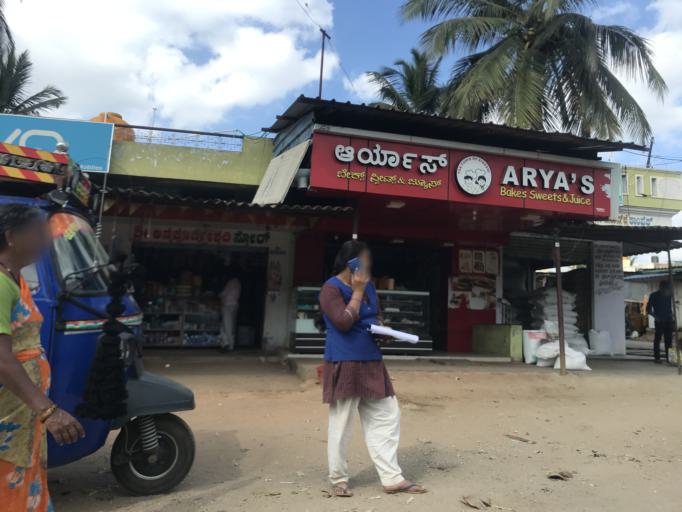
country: IN
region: Karnataka
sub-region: Mandya
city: Krishnarajpet
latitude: 12.7613
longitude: 76.4250
